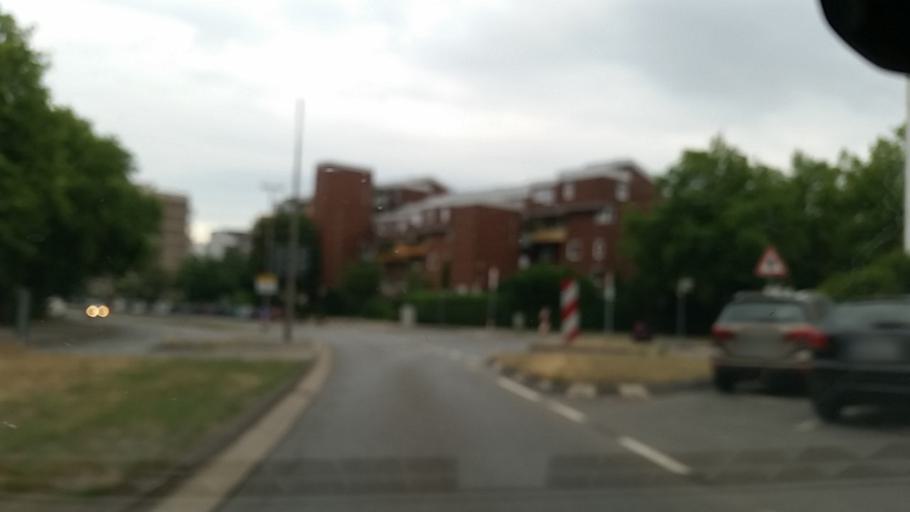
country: DE
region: Lower Saxony
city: Wolfsburg
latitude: 52.3992
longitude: 10.7382
